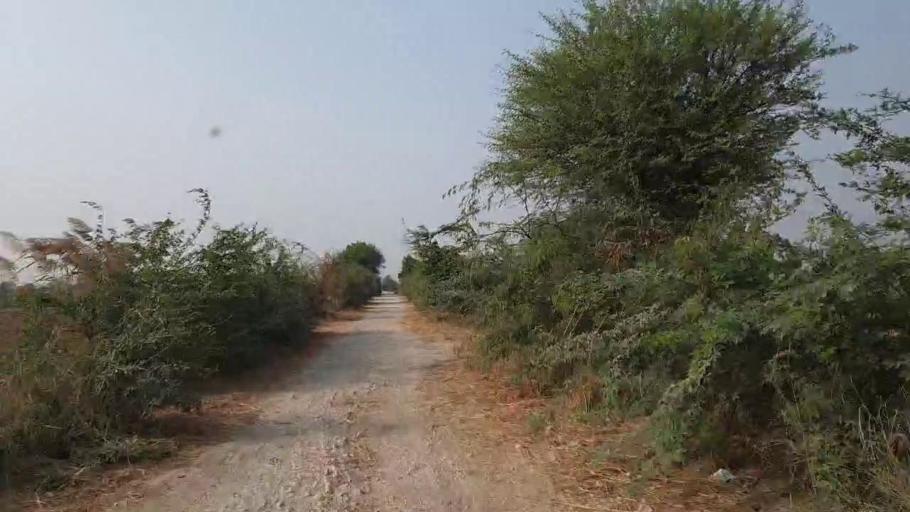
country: PK
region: Sindh
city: Tando Muhammad Khan
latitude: 25.0813
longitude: 68.5877
